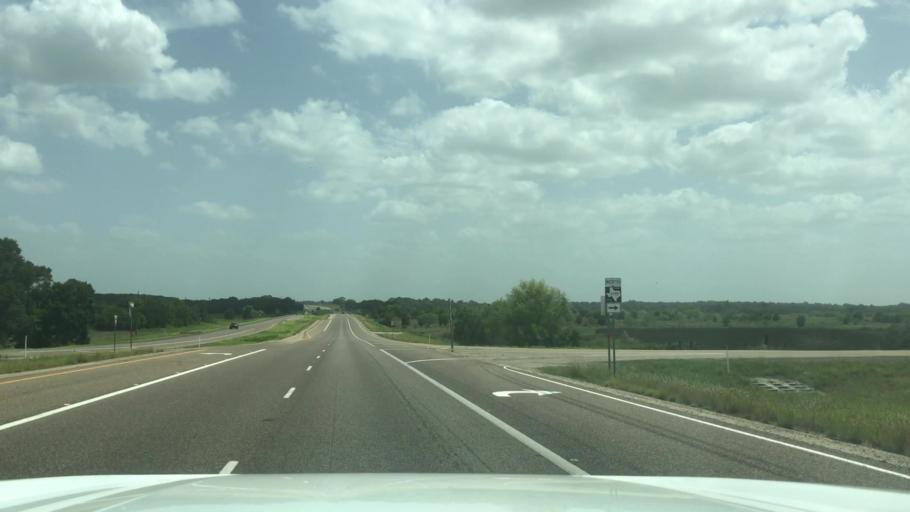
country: US
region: Texas
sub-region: Robertson County
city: Calvert
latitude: 31.0211
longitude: -96.7076
